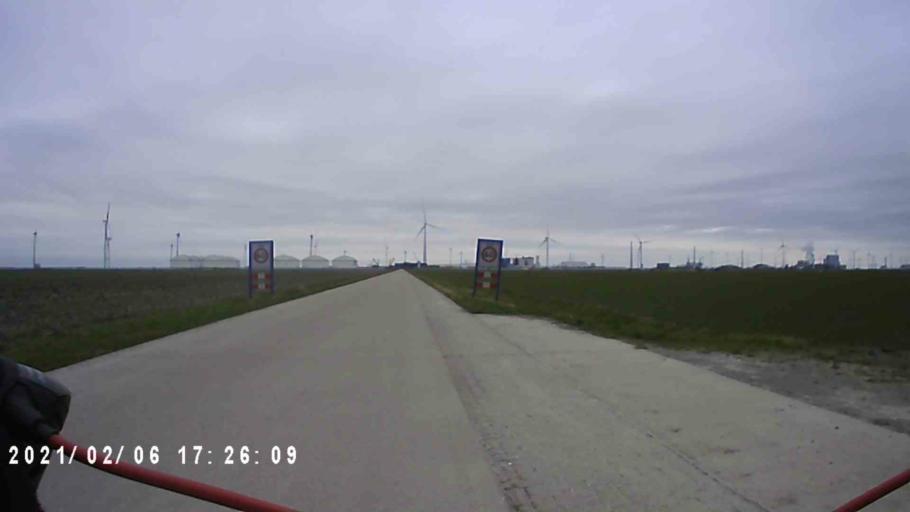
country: NL
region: Groningen
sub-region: Gemeente Appingedam
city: Appingedam
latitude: 53.4383
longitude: 6.7957
